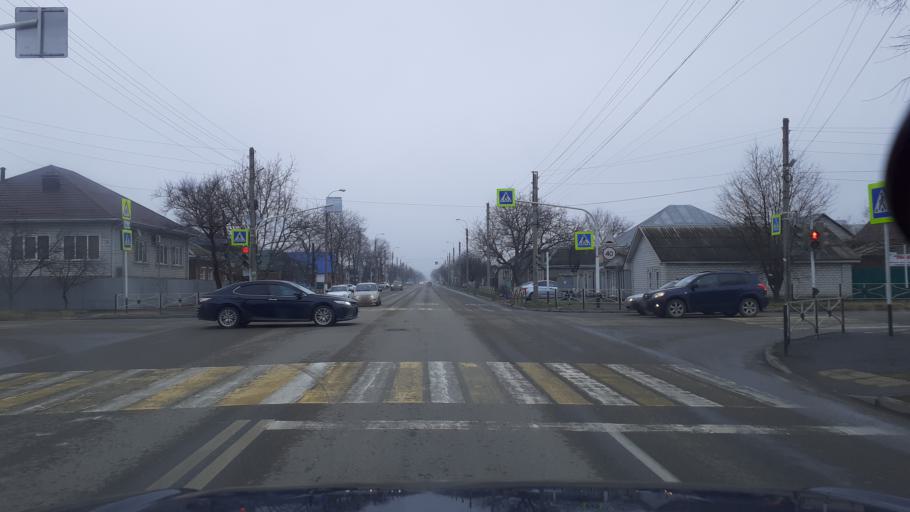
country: RU
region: Adygeya
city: Maykop
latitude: 44.6155
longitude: 40.0778
